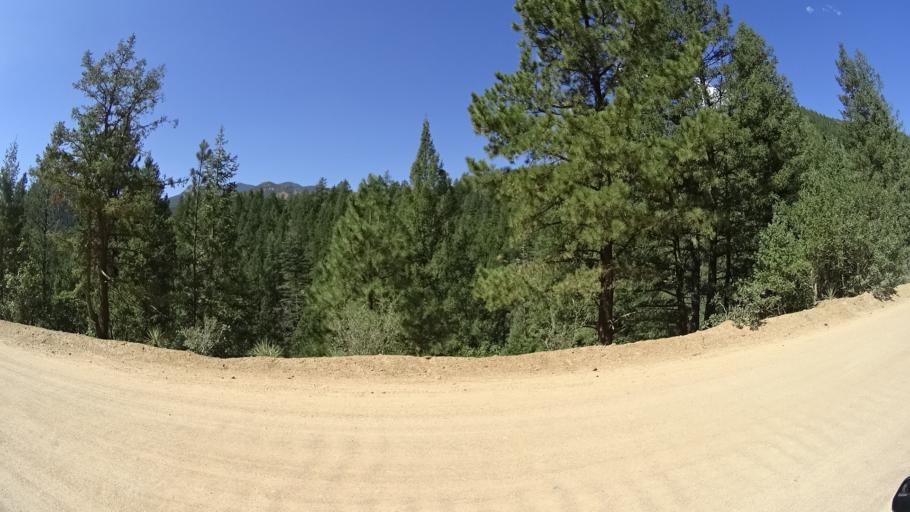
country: US
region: Colorado
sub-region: El Paso County
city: Colorado Springs
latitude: 38.7977
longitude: -104.8825
